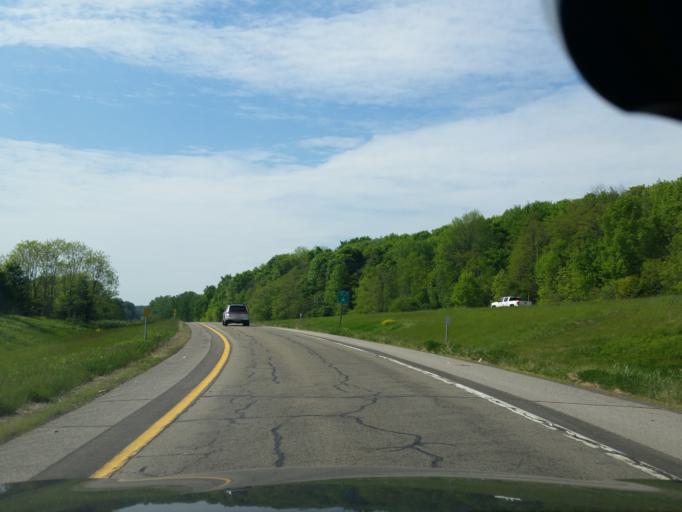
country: US
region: New York
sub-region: Chautauqua County
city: Lakewood
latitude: 42.1555
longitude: -79.3735
